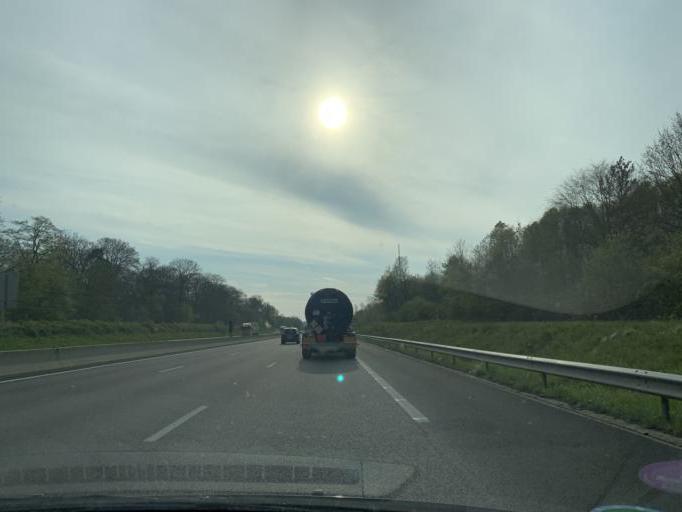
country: FR
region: Haute-Normandie
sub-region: Departement de la Seine-Maritime
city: Cleon
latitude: 49.3426
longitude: 1.0343
